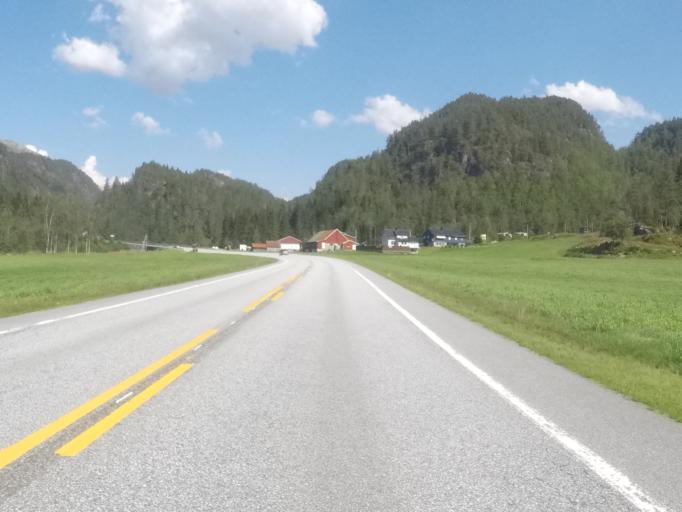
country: NO
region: Hordaland
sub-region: Modalen
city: Mo
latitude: 60.7519
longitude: 5.6281
